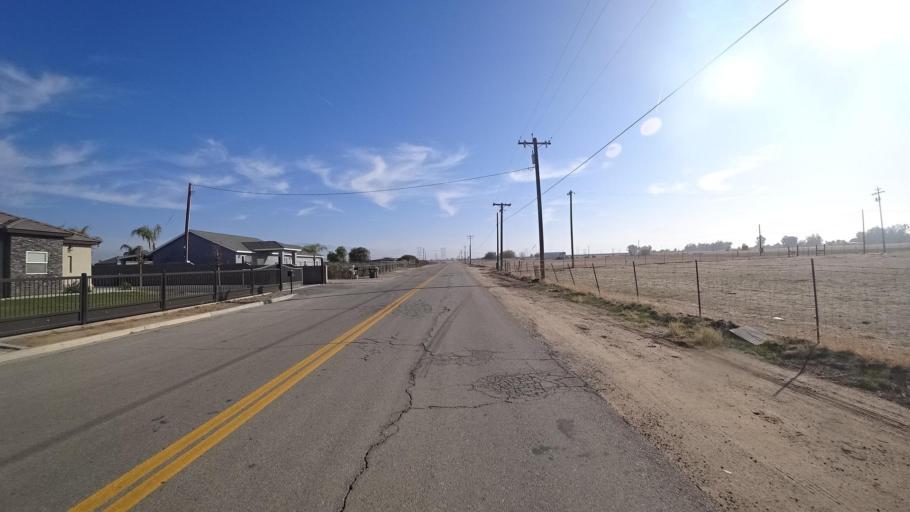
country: US
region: California
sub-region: Kern County
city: Lamont
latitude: 35.3398
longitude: -118.9082
